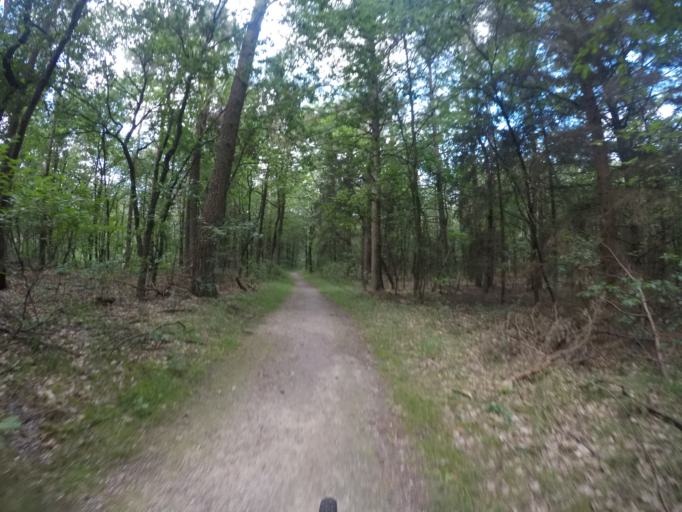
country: NL
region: Drenthe
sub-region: Gemeente Westerveld
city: Dwingeloo
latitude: 52.8881
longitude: 6.3077
